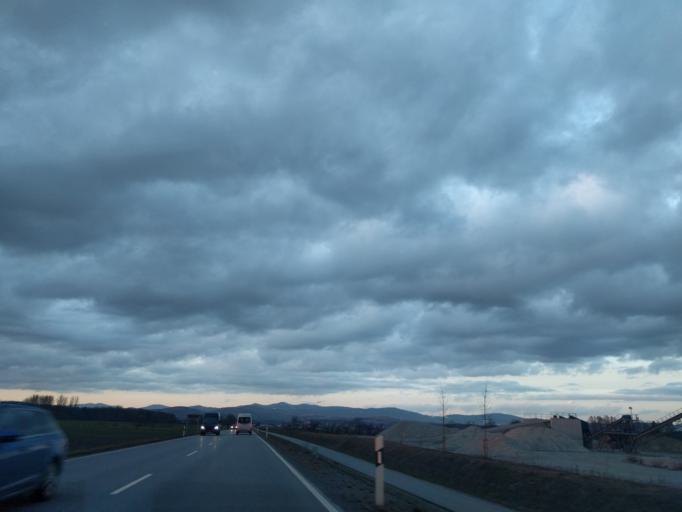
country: DE
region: Bavaria
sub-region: Lower Bavaria
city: Winzer
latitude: 48.7391
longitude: 13.0602
